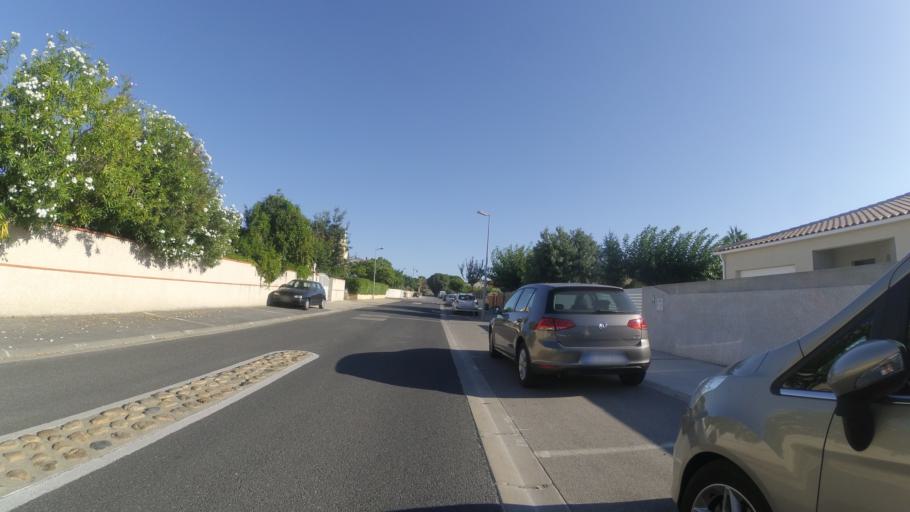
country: FR
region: Languedoc-Roussillon
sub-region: Departement des Pyrenees-Orientales
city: Baho
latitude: 42.7038
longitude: 2.8222
